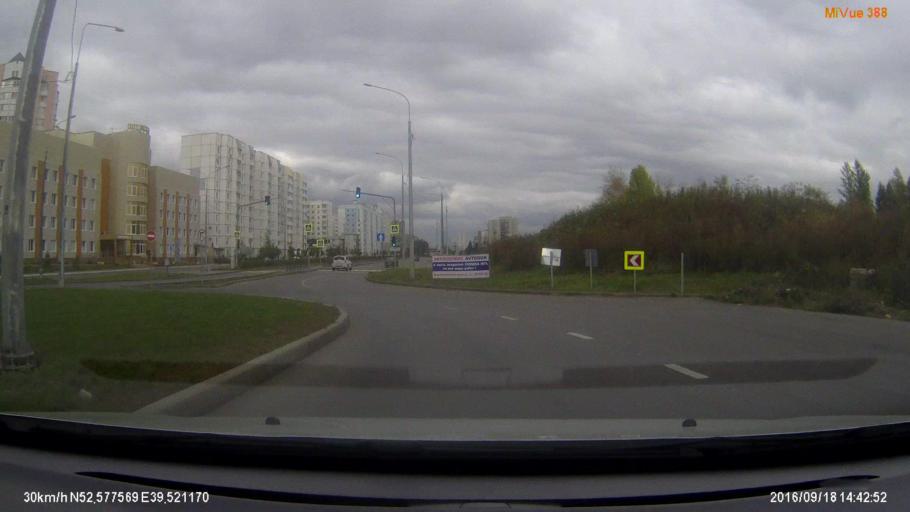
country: RU
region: Lipetsk
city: Syrskoye
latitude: 52.5777
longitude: 39.5214
